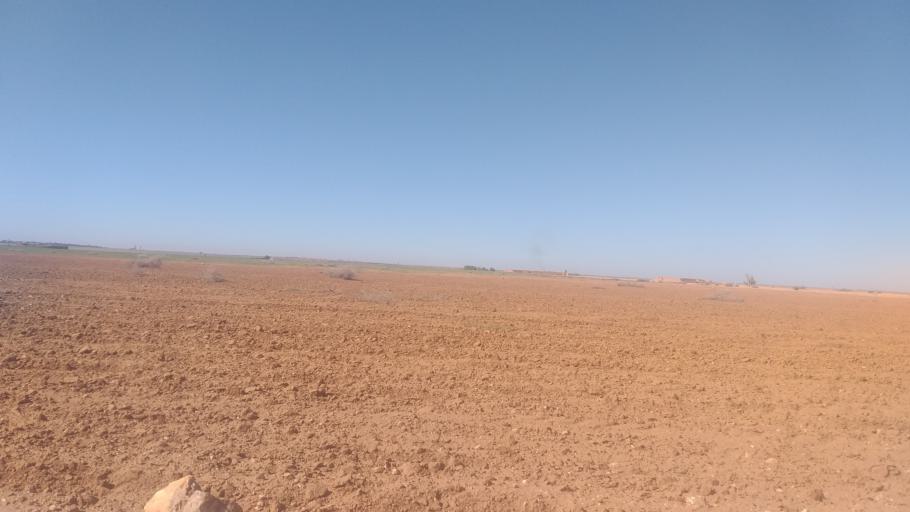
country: MA
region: Marrakech-Tensift-Al Haouz
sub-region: Kelaa-Des-Sraghna
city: Sidi Bou Othmane
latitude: 32.1484
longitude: -7.8595
